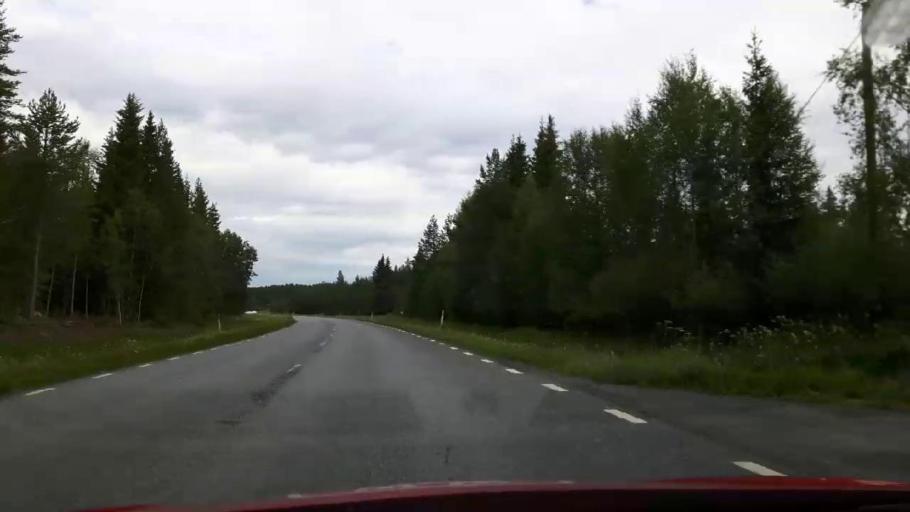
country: SE
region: Jaemtland
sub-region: Stroemsunds Kommun
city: Stroemsund
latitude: 63.5543
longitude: 15.3734
